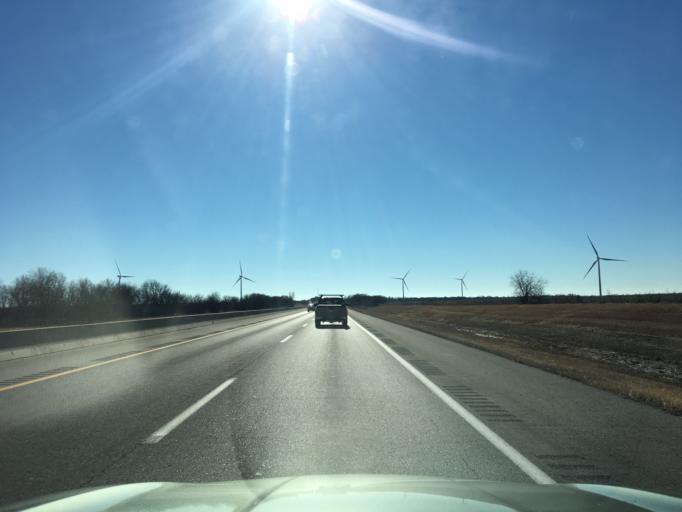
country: US
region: Kansas
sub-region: Sumner County
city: Wellington
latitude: 37.1437
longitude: -97.3395
